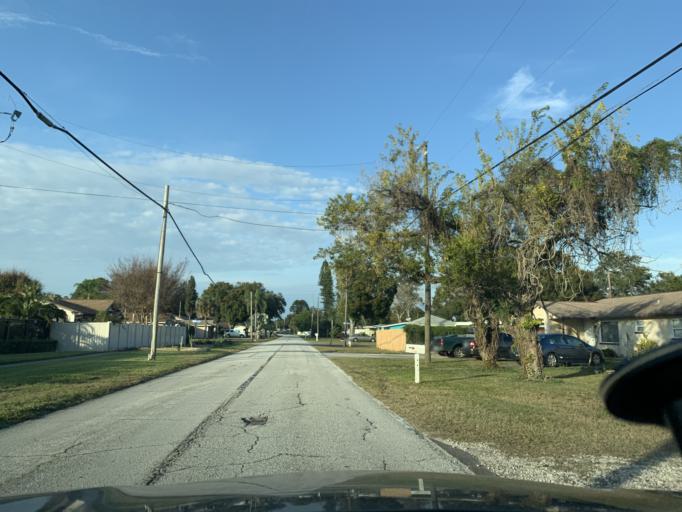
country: US
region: Florida
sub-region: Pinellas County
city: Ridgecrest
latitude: 27.8854
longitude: -82.7976
